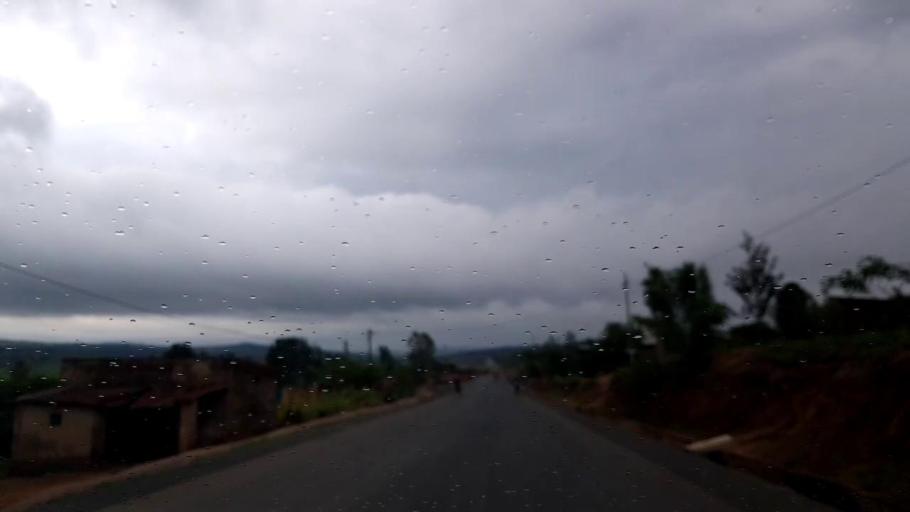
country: RW
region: Northern Province
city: Byumba
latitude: -1.4499
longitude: 30.2454
